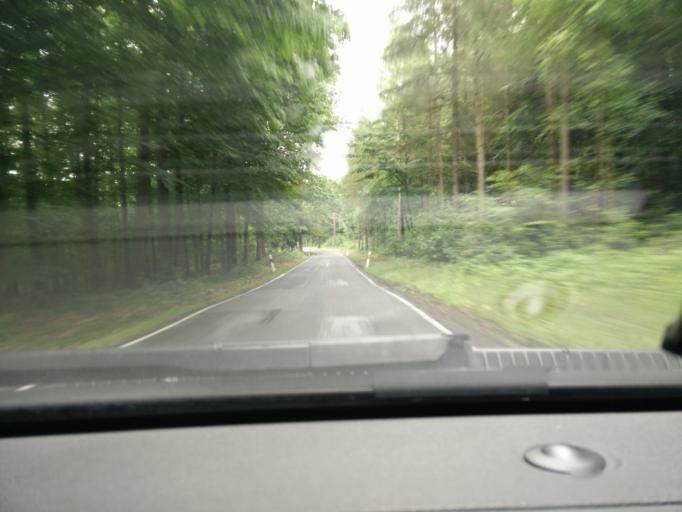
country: DE
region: Saxony
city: Grossbardau
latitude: 51.1688
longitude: 12.7003
